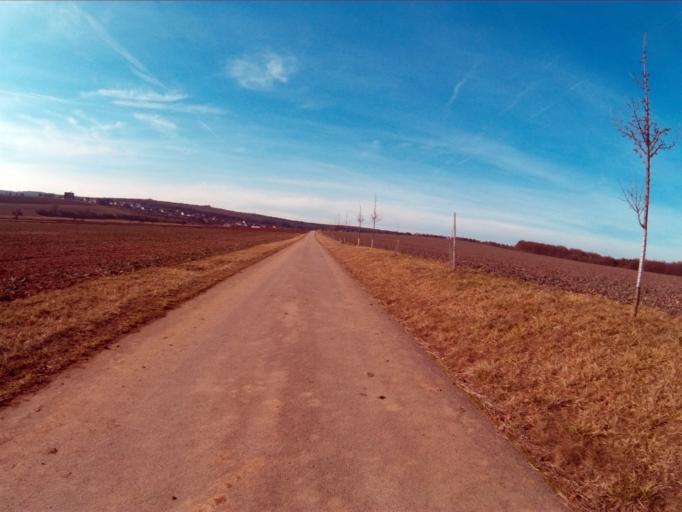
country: CZ
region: Vysocina
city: Mohelno
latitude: 49.1436
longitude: 16.1855
